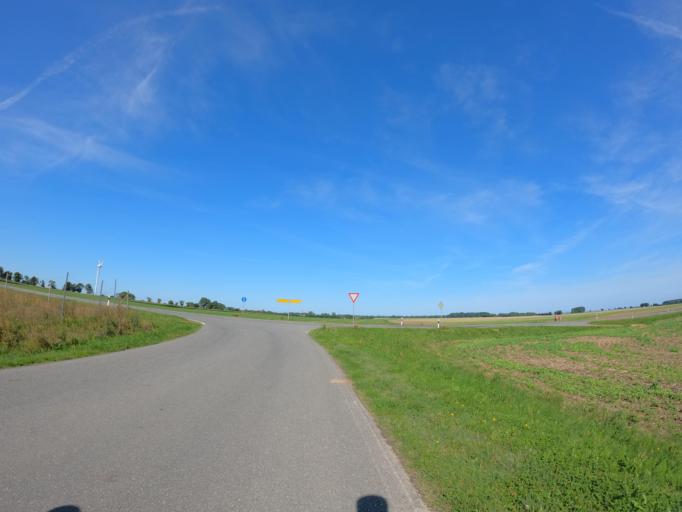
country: DE
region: Mecklenburg-Vorpommern
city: Kramerhof
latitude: 54.3531
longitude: 13.0476
